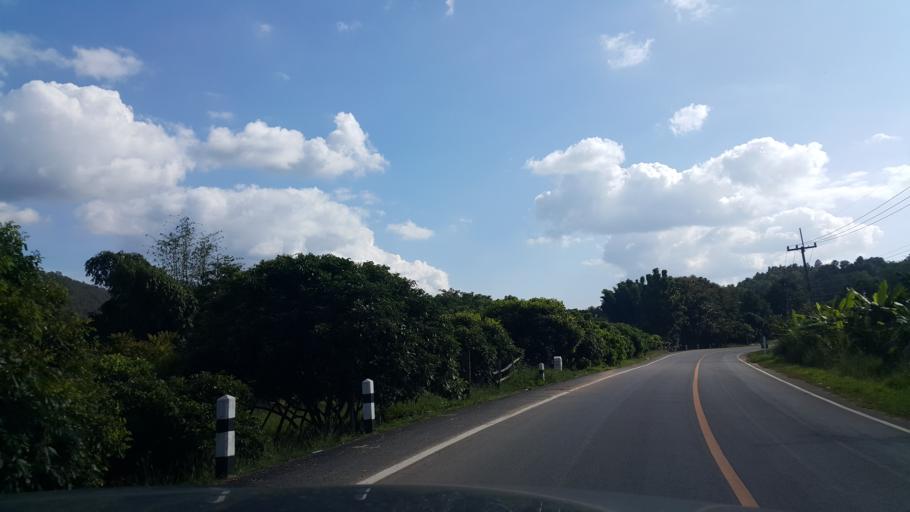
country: TH
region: Lamphun
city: Ban Thi
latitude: 18.5720
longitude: 99.2574
